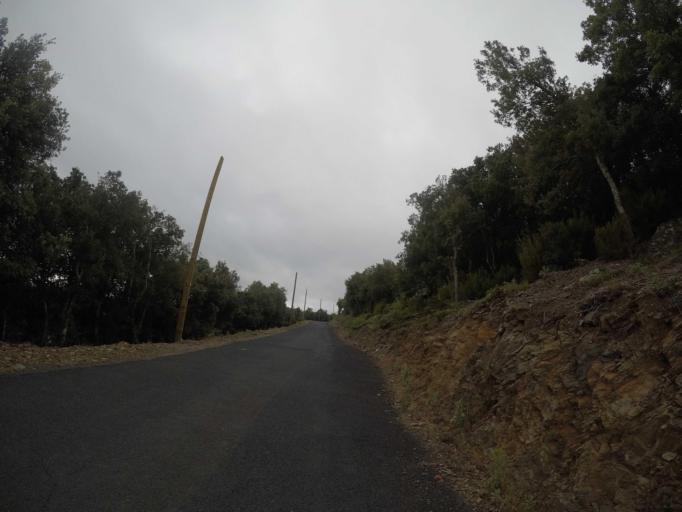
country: FR
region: Languedoc-Roussillon
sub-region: Departement des Pyrenees-Orientales
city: Ille-sur-Tet
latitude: 42.6221
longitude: 2.6204
